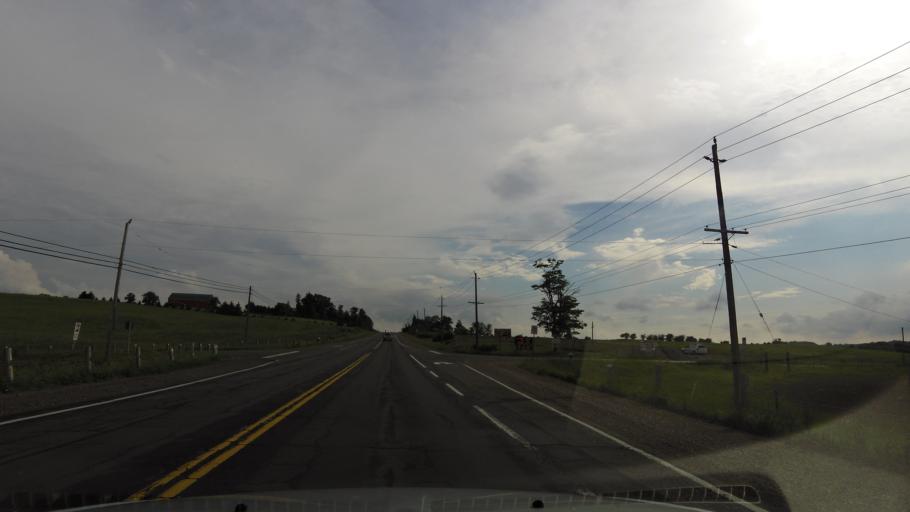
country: CA
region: Ontario
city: Ancaster
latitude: 43.0398
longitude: -79.9817
